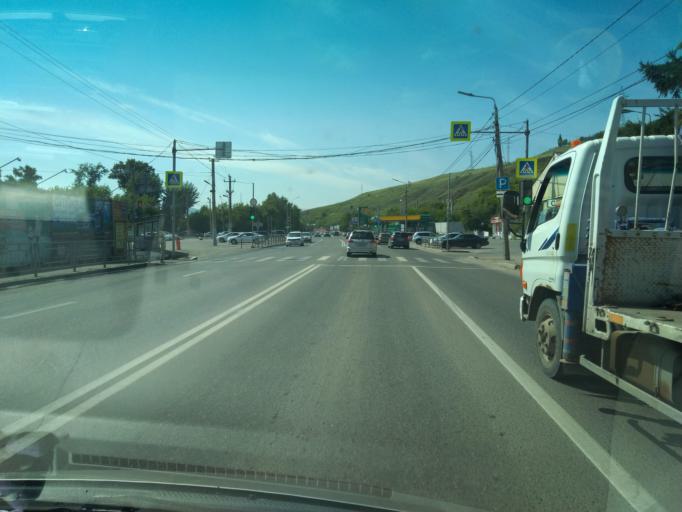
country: RU
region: Krasnoyarskiy
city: Krasnoyarsk
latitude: 56.0207
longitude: 92.8706
